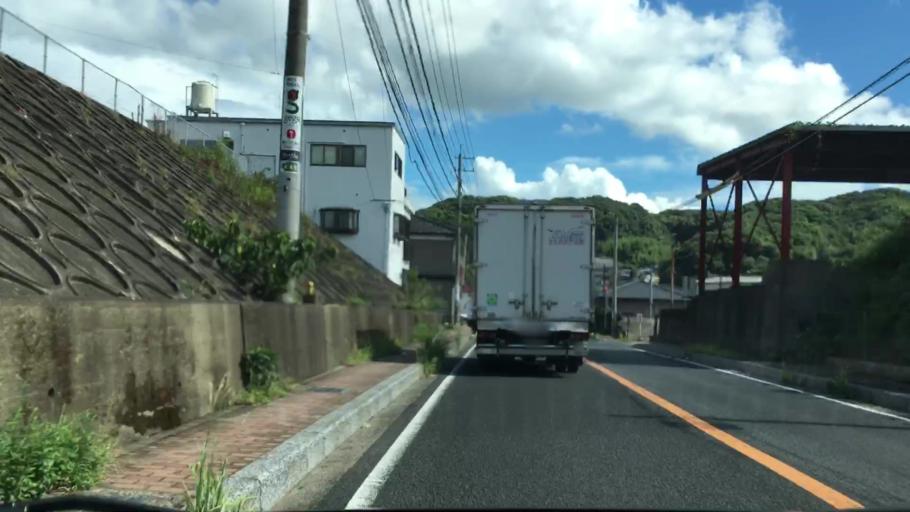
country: JP
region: Nagasaki
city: Sasebo
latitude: 33.1412
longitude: 129.7872
